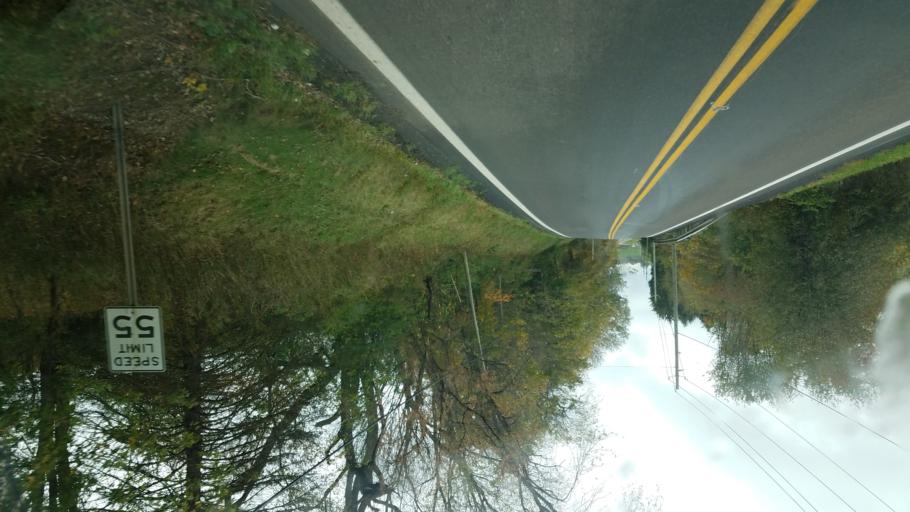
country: US
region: Ohio
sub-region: Holmes County
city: Millersburg
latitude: 40.6075
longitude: -81.8394
